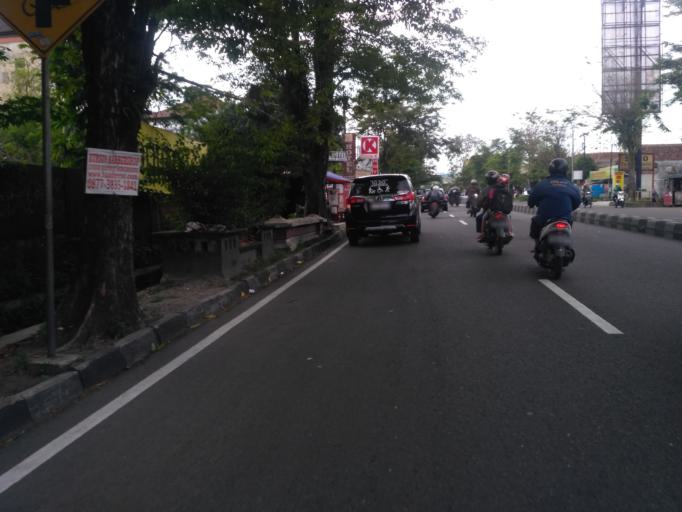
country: ID
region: Daerah Istimewa Yogyakarta
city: Melati
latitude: -7.7434
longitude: 110.3626
